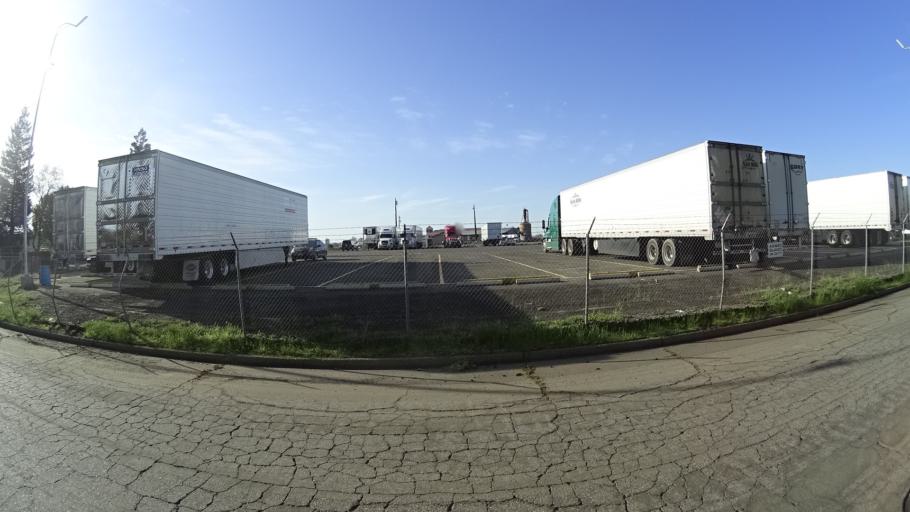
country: US
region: California
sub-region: Fresno County
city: West Park
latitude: 36.8137
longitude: -119.8812
